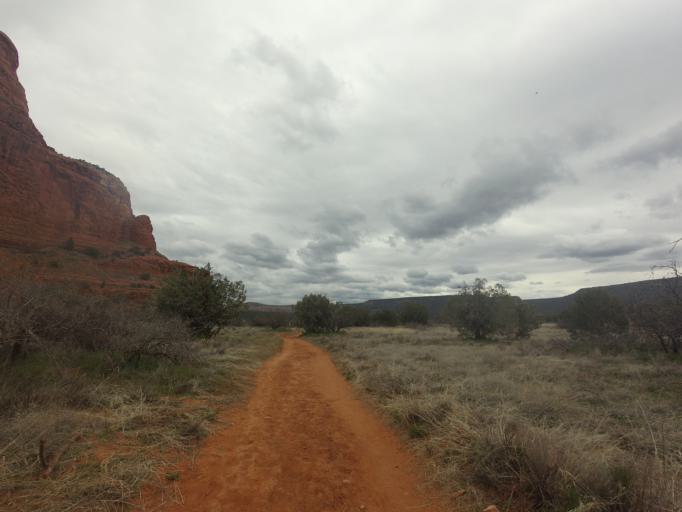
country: US
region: Arizona
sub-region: Yavapai County
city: Village of Oak Creek (Big Park)
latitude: 34.7978
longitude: -111.7592
